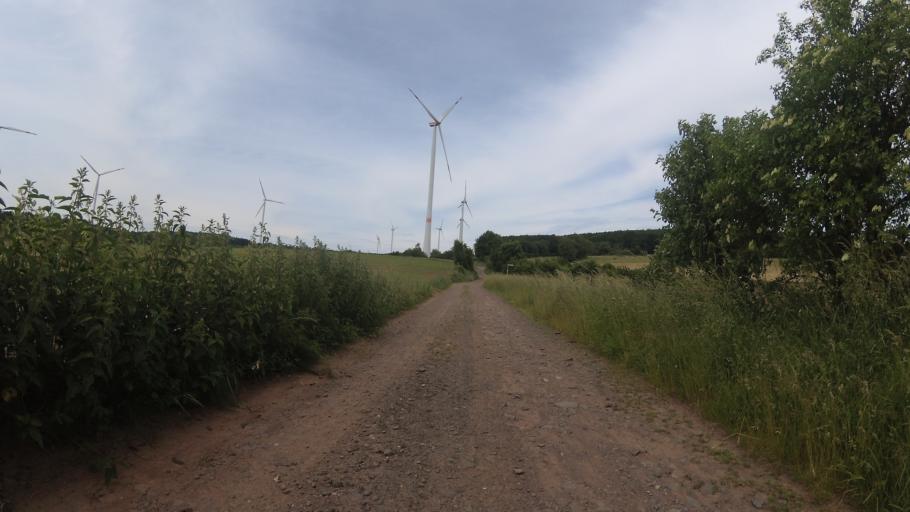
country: DE
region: Rheinland-Pfalz
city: Breitenbach
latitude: 49.4317
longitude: 7.2233
